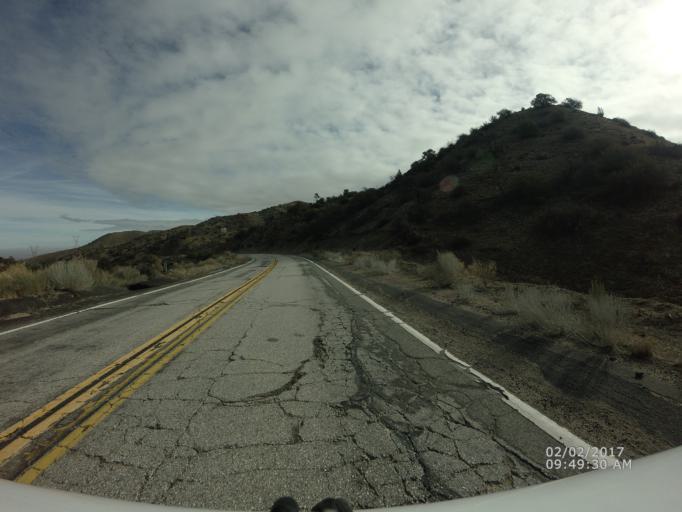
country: US
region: California
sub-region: Los Angeles County
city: Vincent
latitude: 34.4813
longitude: -118.0677
